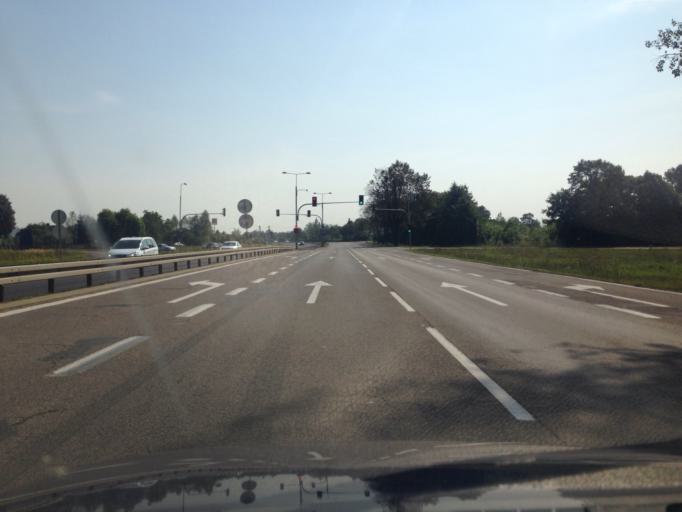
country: PL
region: Masovian Voivodeship
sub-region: Powiat plonski
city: Plonsk
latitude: 52.5892
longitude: 20.4498
